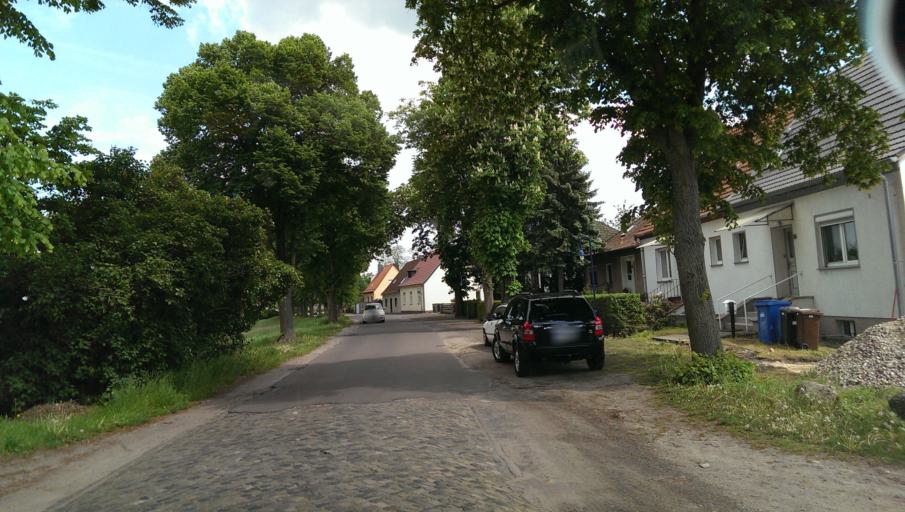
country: DE
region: Brandenburg
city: Ziesar
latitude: 52.2639
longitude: 12.2836
